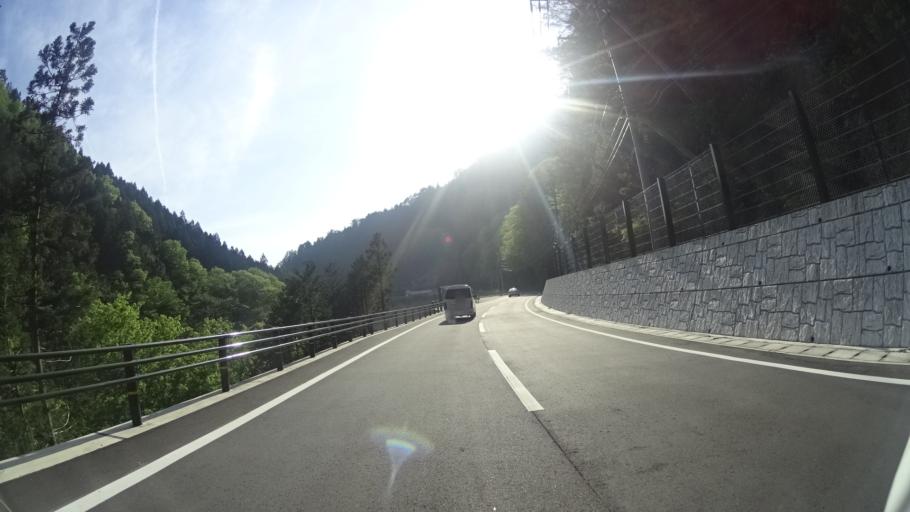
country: JP
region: Tokushima
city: Ikedacho
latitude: 33.8738
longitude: 133.9197
